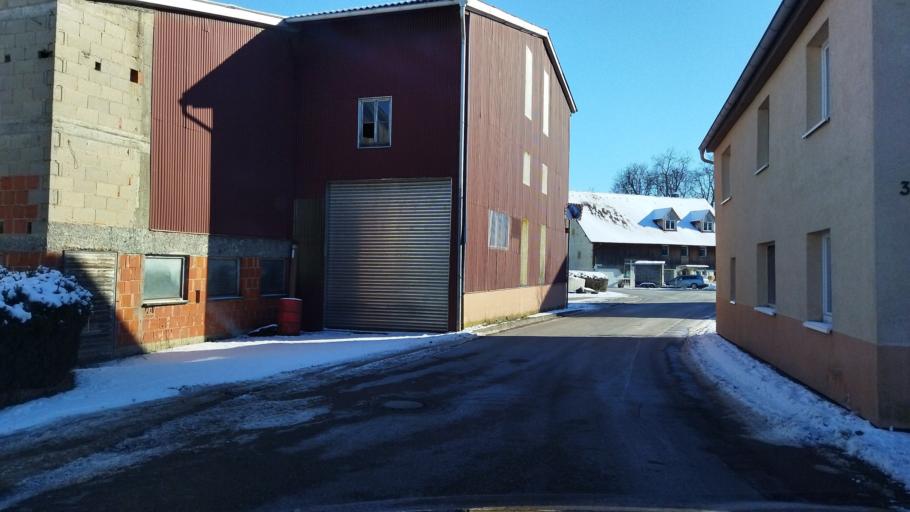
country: DE
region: Baden-Wuerttemberg
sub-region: Regierungsbezirk Stuttgart
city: Ilshofen
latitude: 49.2002
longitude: 9.9347
